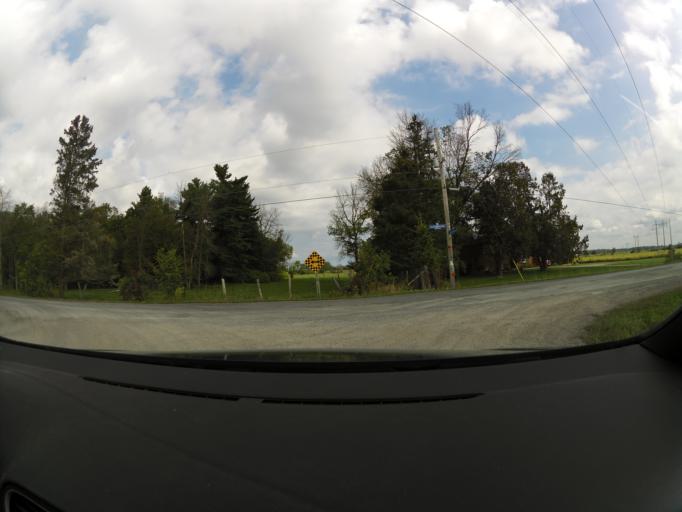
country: CA
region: Ontario
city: Arnprior
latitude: 45.4119
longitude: -76.2153
